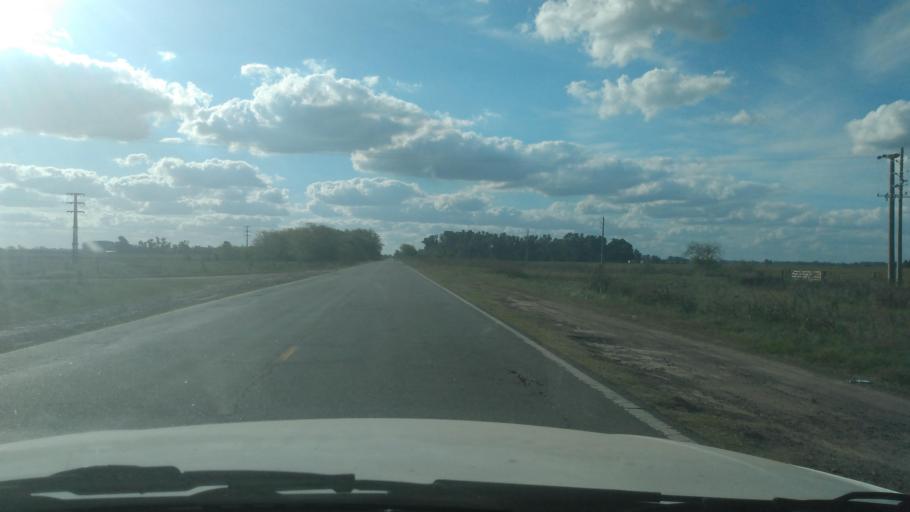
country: AR
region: Buenos Aires
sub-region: Partido de Mercedes
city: Mercedes
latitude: -34.7578
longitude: -59.3773
